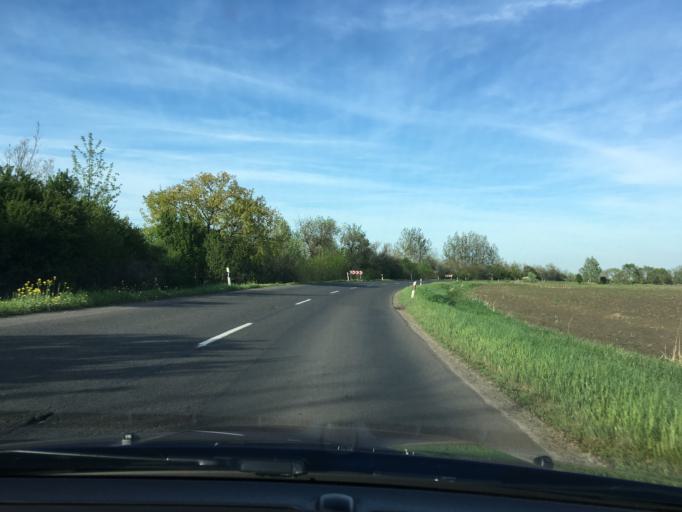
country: HU
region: Bekes
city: Korostarcsa
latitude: 46.9181
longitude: 21.0596
